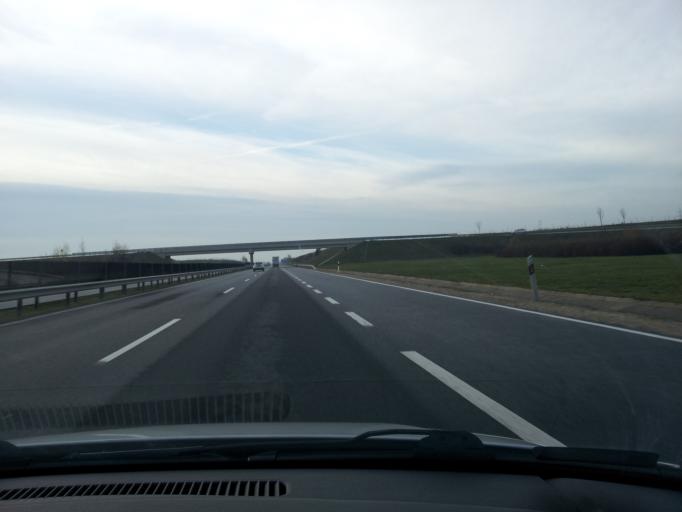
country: HU
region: Fejer
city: Rackeresztur
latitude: 47.3072
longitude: 18.8675
